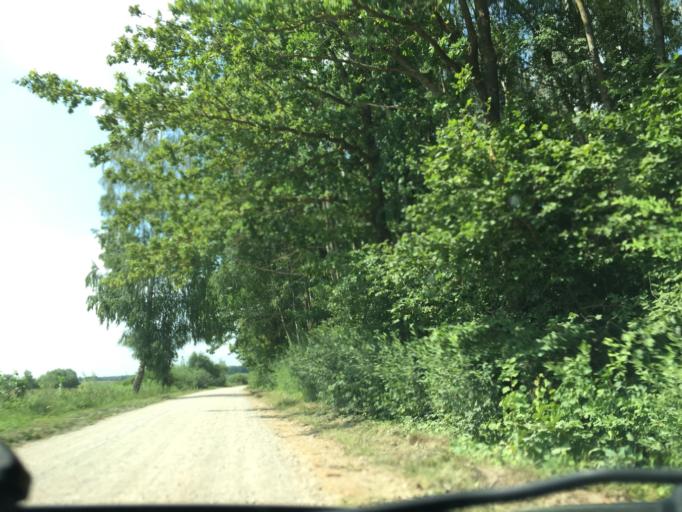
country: LT
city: Zagare
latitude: 56.3895
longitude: 23.2598
